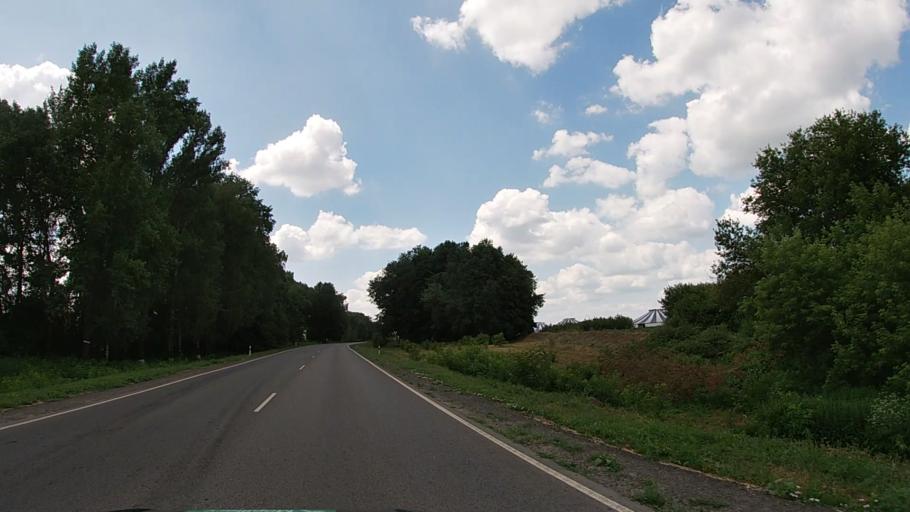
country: RU
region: Belgorod
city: Grayvoron
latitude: 50.4961
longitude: 35.7133
